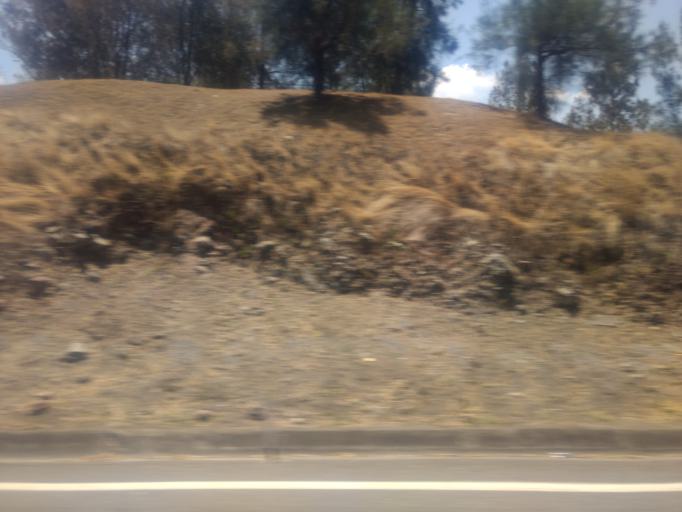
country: MX
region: Colima
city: Queseria
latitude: 19.3645
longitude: -103.5633
